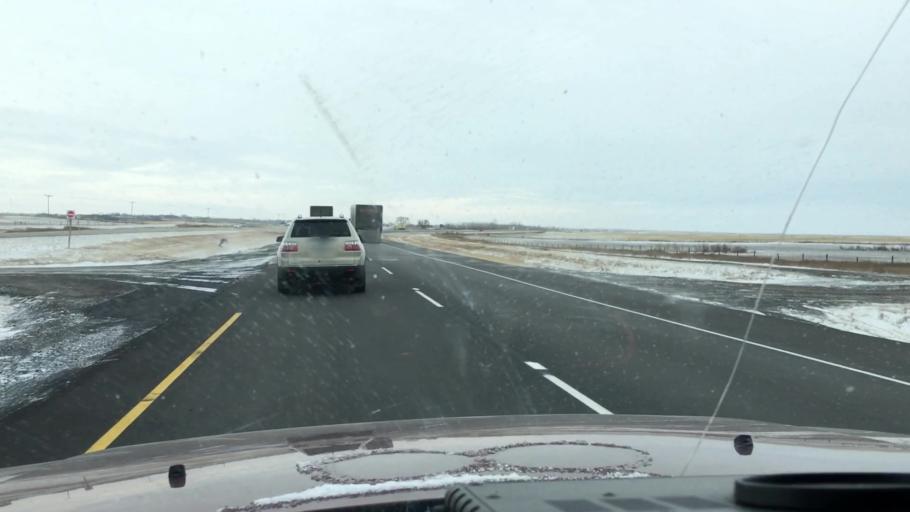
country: CA
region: Saskatchewan
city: Saskatoon
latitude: 51.7825
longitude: -106.4784
